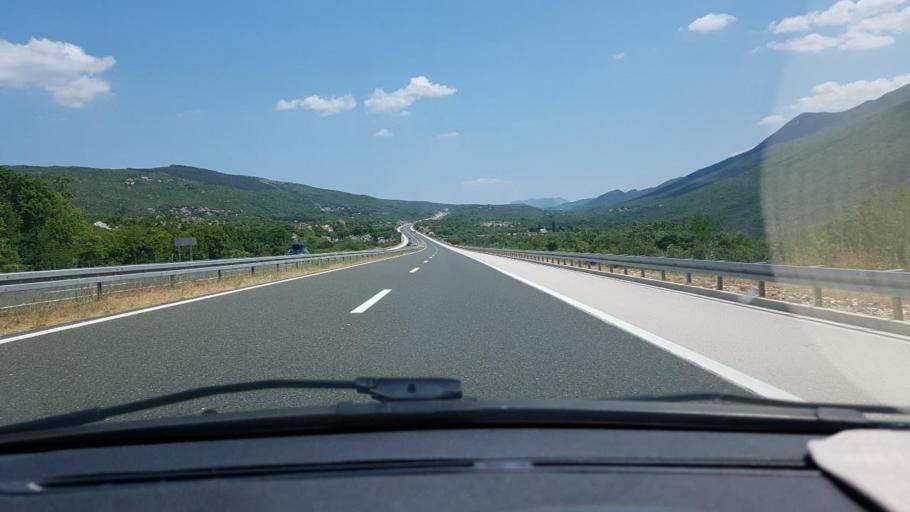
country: HR
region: Splitsko-Dalmatinska
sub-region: Grad Makarska
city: Makarska
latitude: 43.3936
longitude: 17.0460
